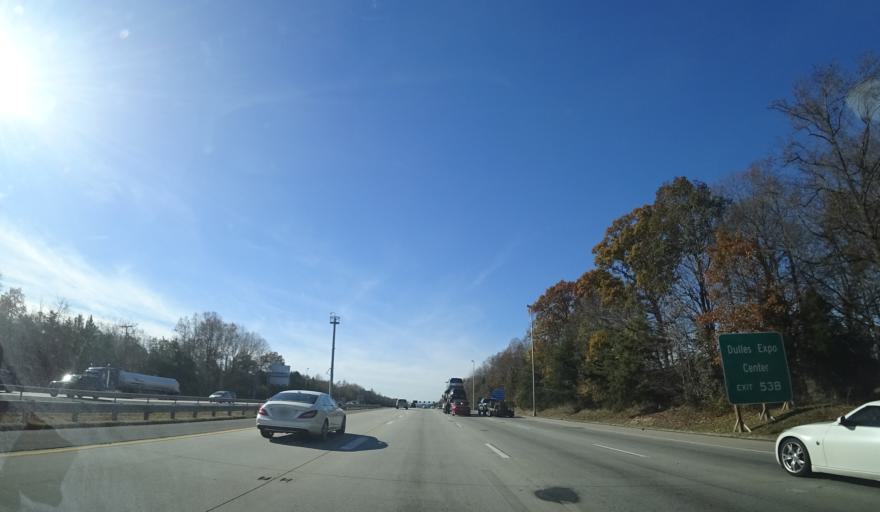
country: US
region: Virginia
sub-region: Fairfax County
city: Centreville
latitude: 38.8491
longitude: -77.4194
